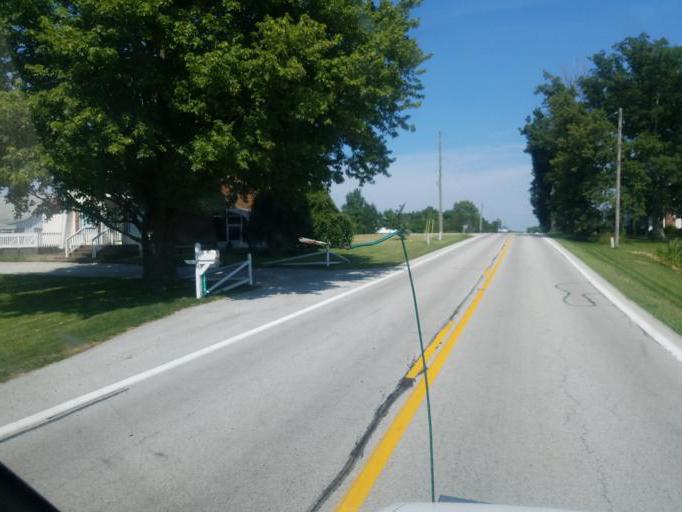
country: US
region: Ohio
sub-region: Shelby County
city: Botkins
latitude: 40.4967
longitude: -84.2196
